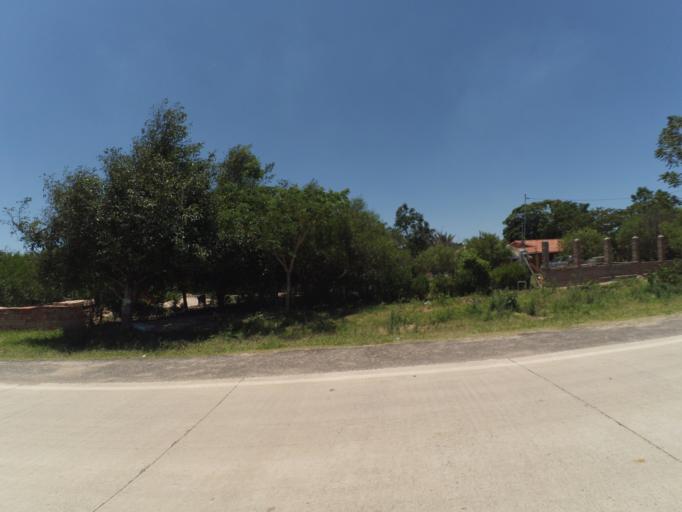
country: BO
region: Santa Cruz
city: Santa Cruz de la Sierra
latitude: -17.8437
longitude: -63.2999
